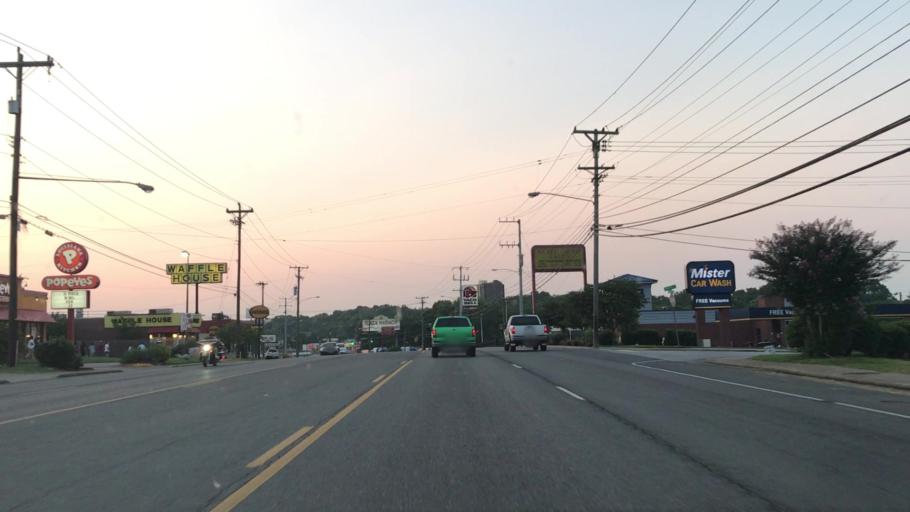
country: US
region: Tennessee
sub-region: Davidson County
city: Oak Hill
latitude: 36.0830
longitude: -86.7273
